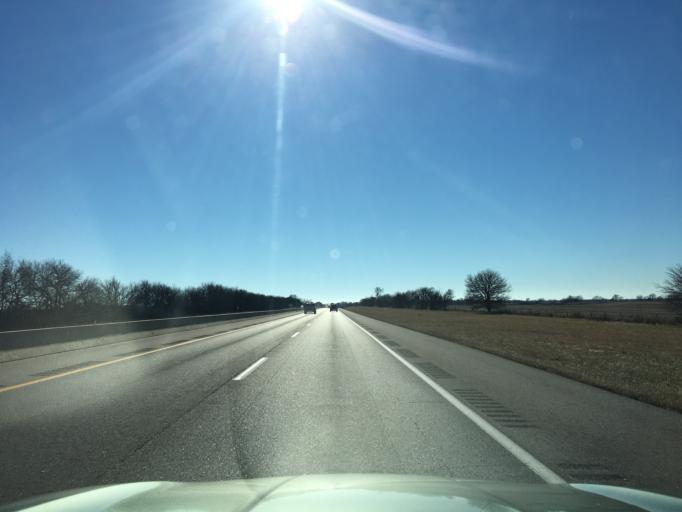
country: US
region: Kansas
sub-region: Sumner County
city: Wellington
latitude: 37.1015
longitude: -97.3388
